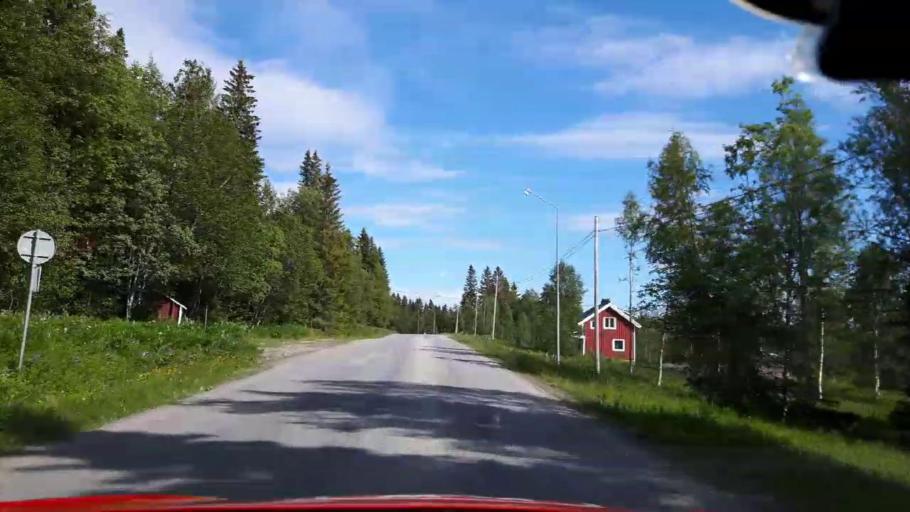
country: SE
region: Jaemtland
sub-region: Krokoms Kommun
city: Valla
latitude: 63.7702
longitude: 14.0541
